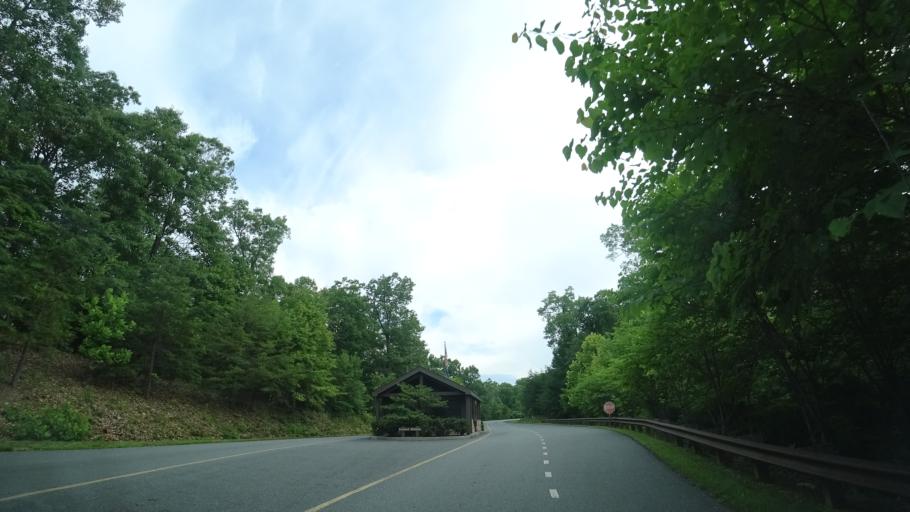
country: US
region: Virginia
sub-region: Warren County
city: Front Royal
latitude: 38.8446
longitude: -78.3016
